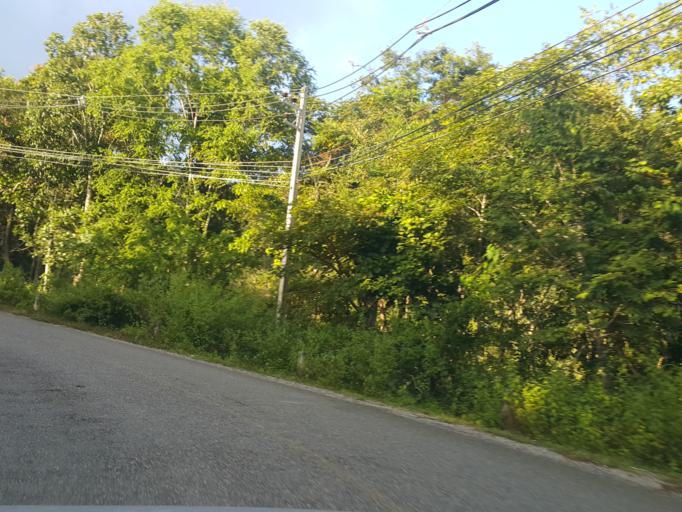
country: TH
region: Chiang Mai
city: Mae Chaem
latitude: 18.7419
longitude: 98.2226
